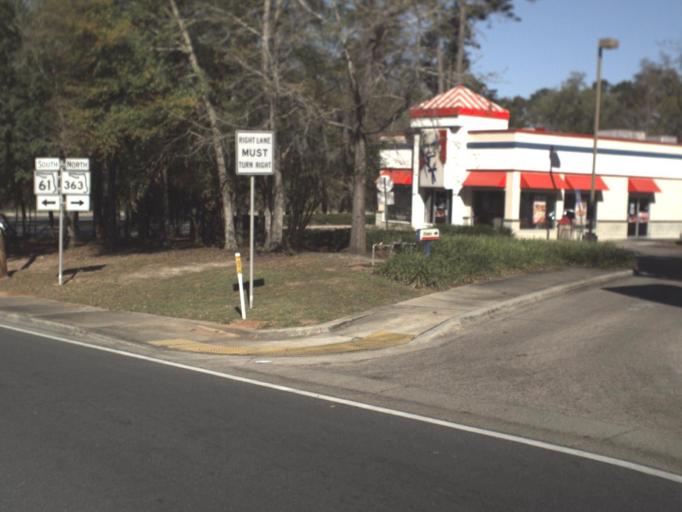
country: US
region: Florida
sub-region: Leon County
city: Tallahassee
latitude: 30.4053
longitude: -84.2829
